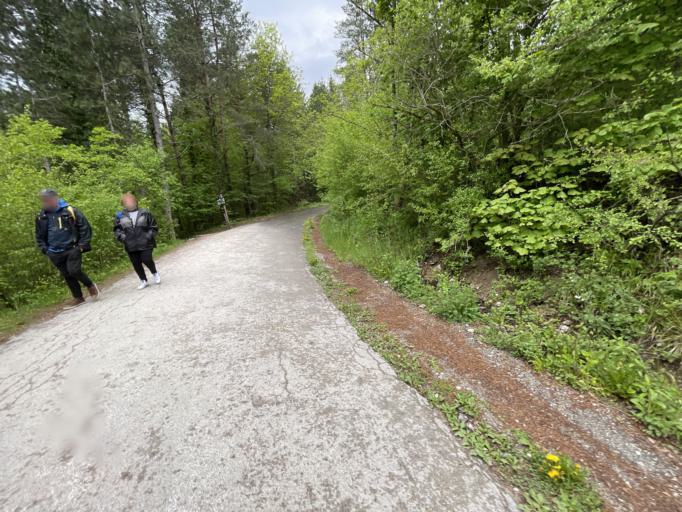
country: HR
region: Licko-Senjska
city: Jezerce
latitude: 44.8937
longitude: 15.6069
